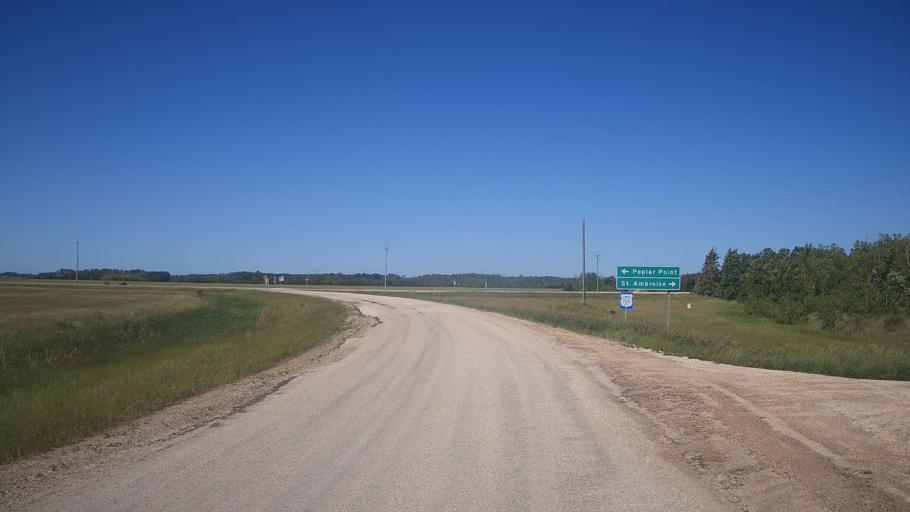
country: CA
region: Manitoba
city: Portage la Prairie
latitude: 50.2410
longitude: -98.0328
